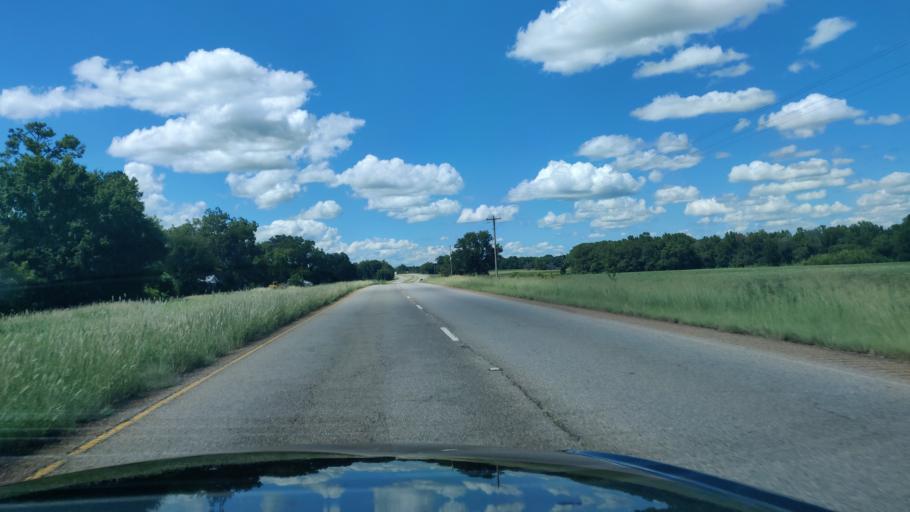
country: US
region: Georgia
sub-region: Stewart County
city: Richland
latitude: 32.0634
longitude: -84.6715
